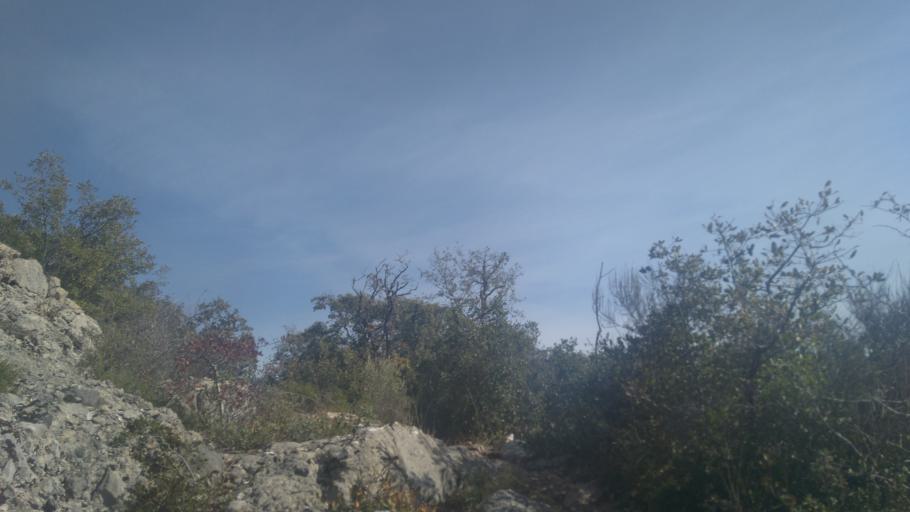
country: PT
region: Leiria
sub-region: Alcobaca
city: Aljubarrota
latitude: 39.5233
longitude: -8.8629
